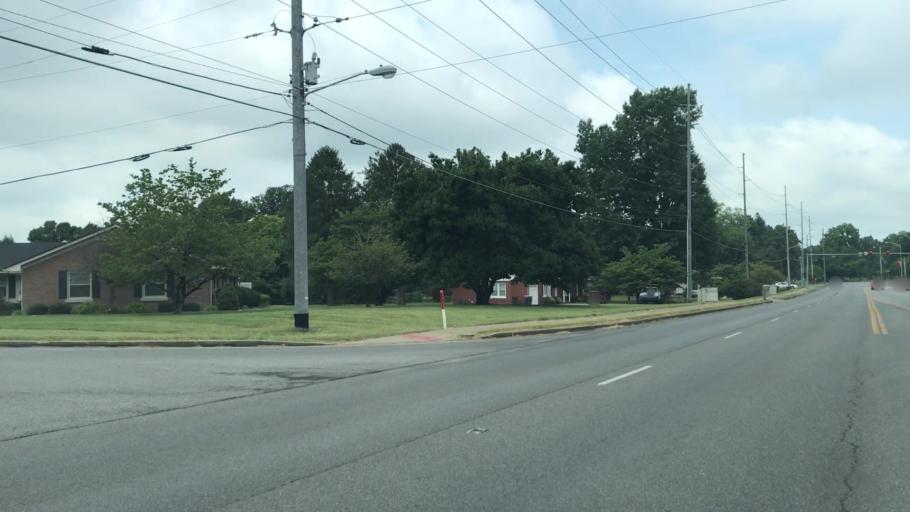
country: US
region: Kentucky
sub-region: Warren County
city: Bowling Green
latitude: 36.9901
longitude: -86.4157
